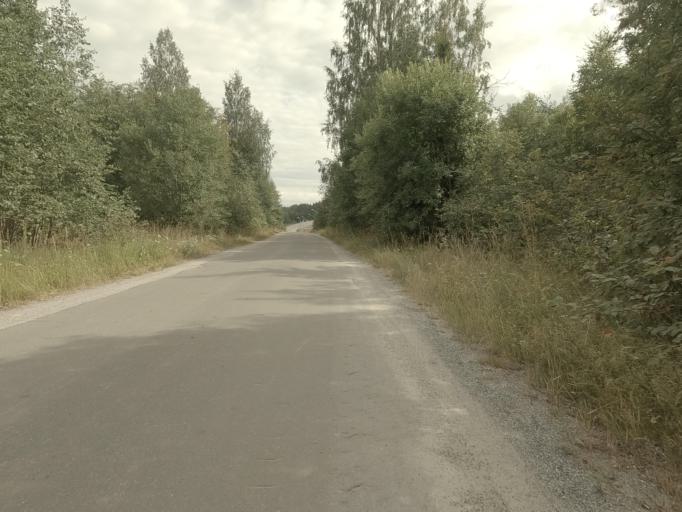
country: RU
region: Leningrad
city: Kamennogorsk
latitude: 60.9681
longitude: 29.1382
